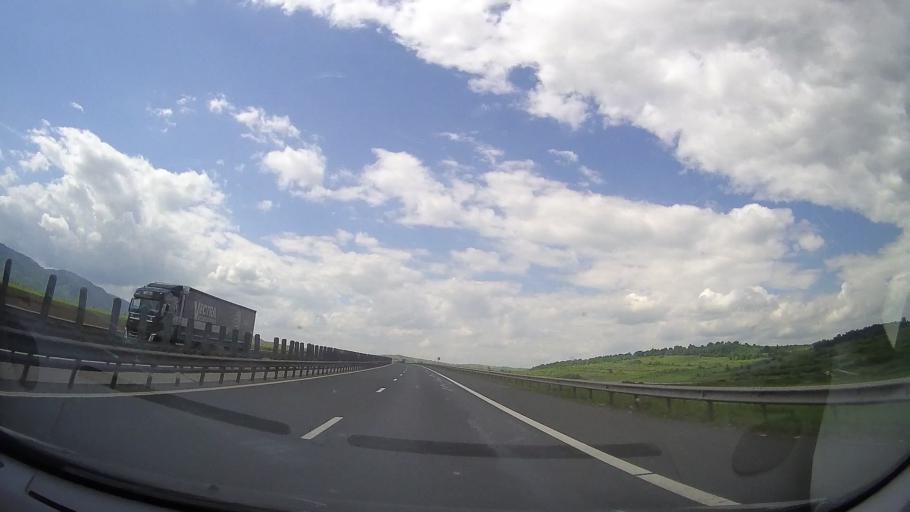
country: RO
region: Sibiu
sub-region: Oras Saliste
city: Saliste
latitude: 45.7947
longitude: 23.9364
